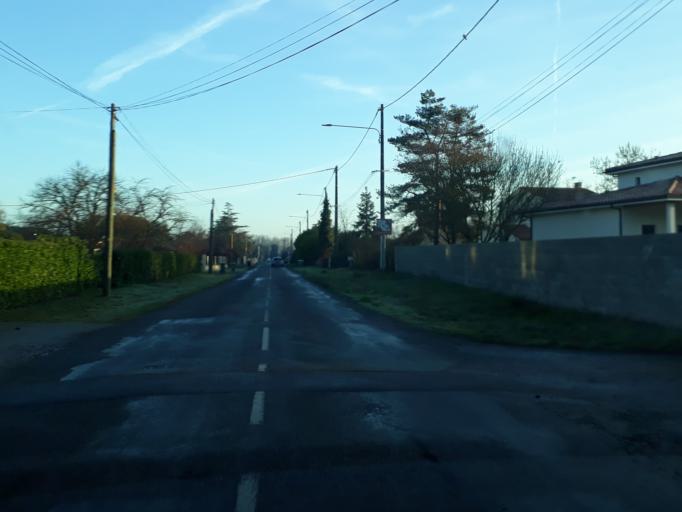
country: FR
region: Midi-Pyrenees
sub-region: Departement de la Haute-Garonne
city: Longages
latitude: 43.3442
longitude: 1.2341
